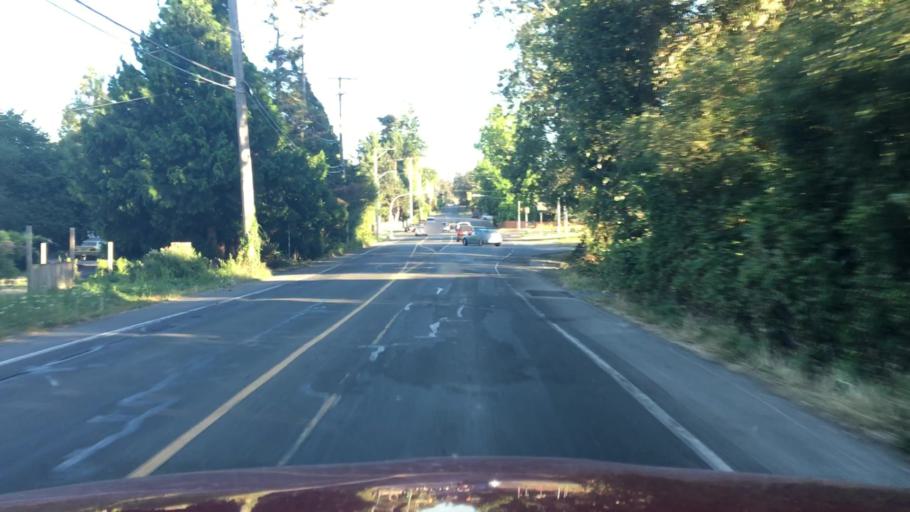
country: CA
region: British Columbia
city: Victoria
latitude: 48.4731
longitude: -123.3516
